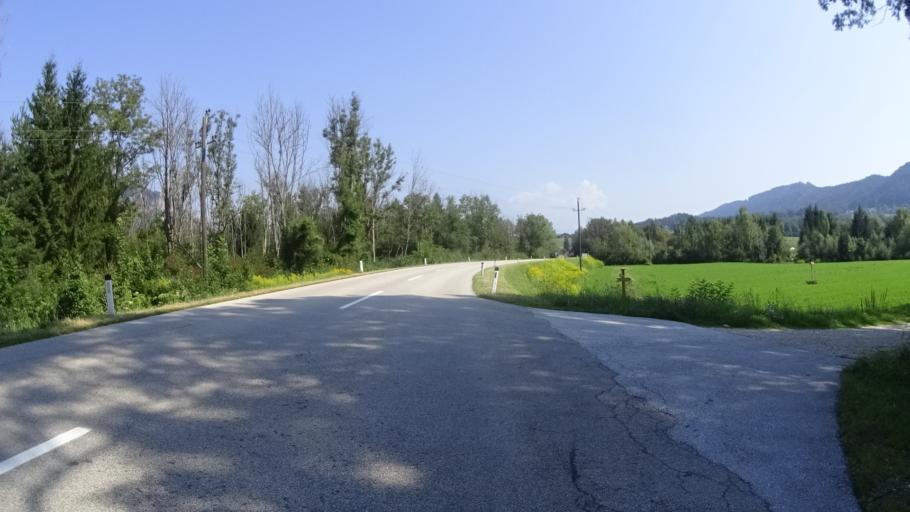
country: AT
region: Carinthia
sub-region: Politischer Bezirk Volkermarkt
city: Gallizien
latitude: 46.5686
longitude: 14.5063
